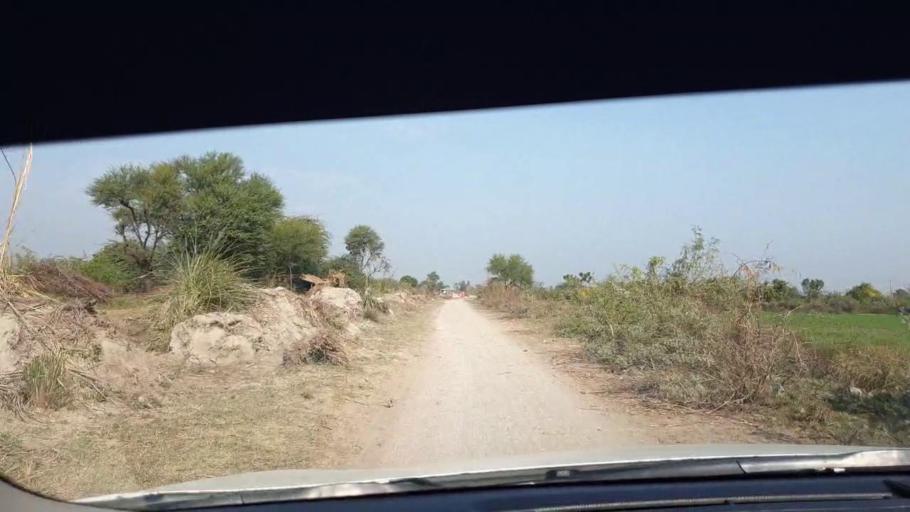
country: PK
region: Sindh
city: Tando Adam
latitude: 25.7333
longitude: 68.7025
